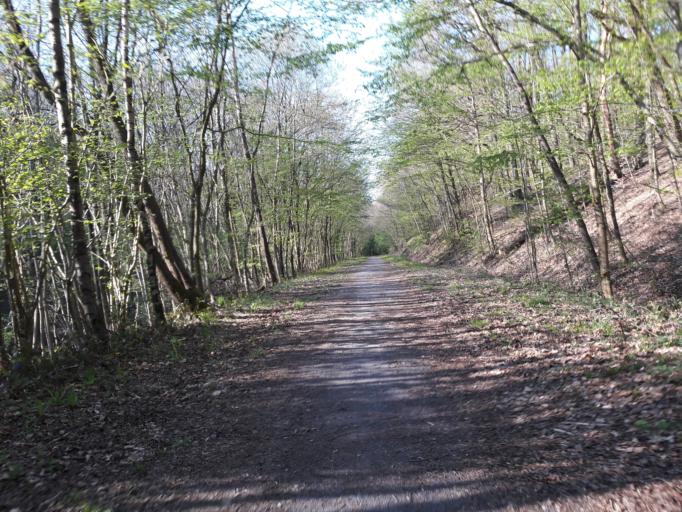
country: FR
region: Nord-Pas-de-Calais
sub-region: Departement du Nord
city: Sains-du-Nord
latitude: 50.1352
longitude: 4.0663
